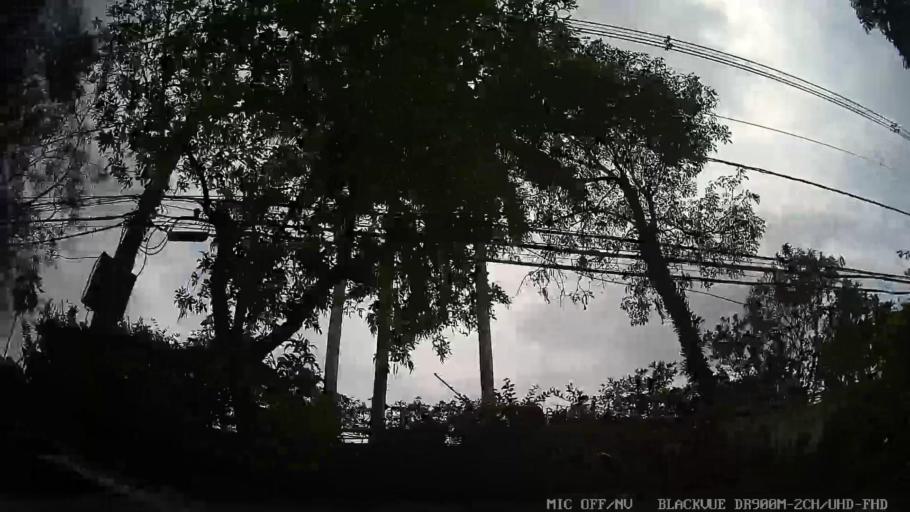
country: BR
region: Sao Paulo
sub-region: Diadema
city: Diadema
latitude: -23.6345
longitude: -46.6731
